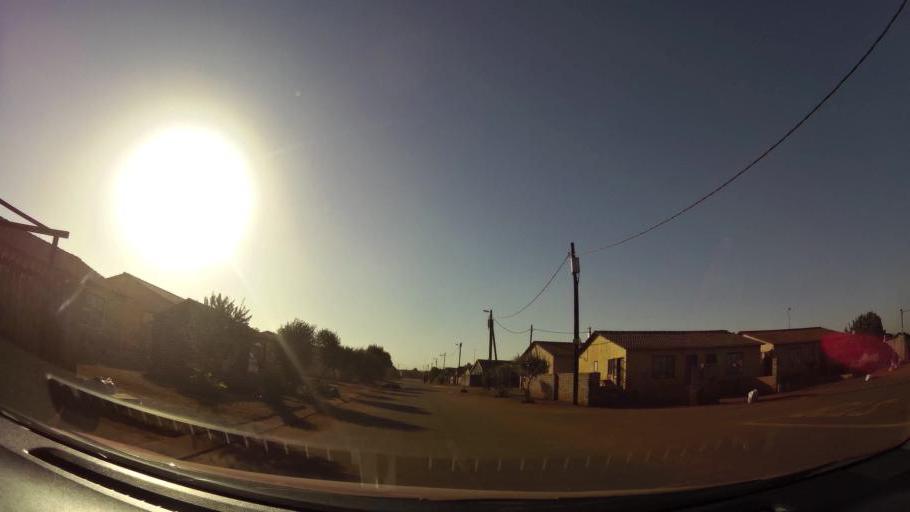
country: ZA
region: Gauteng
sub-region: City of Tshwane Metropolitan Municipality
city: Mabopane
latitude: -25.5902
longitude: 28.0951
